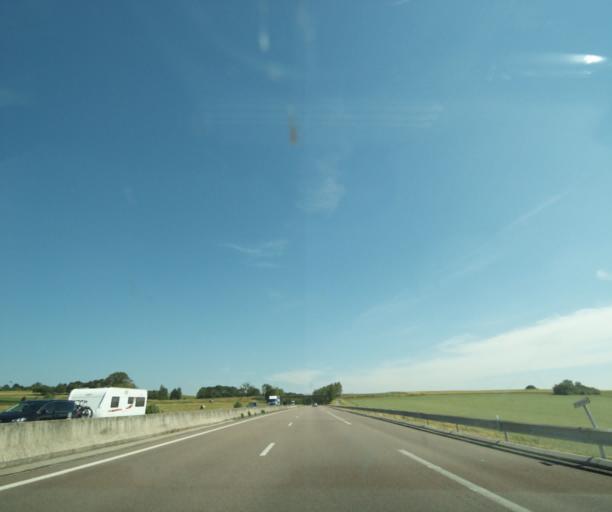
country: FR
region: Lorraine
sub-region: Departement des Vosges
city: Chatenois
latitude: 48.3947
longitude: 5.8803
